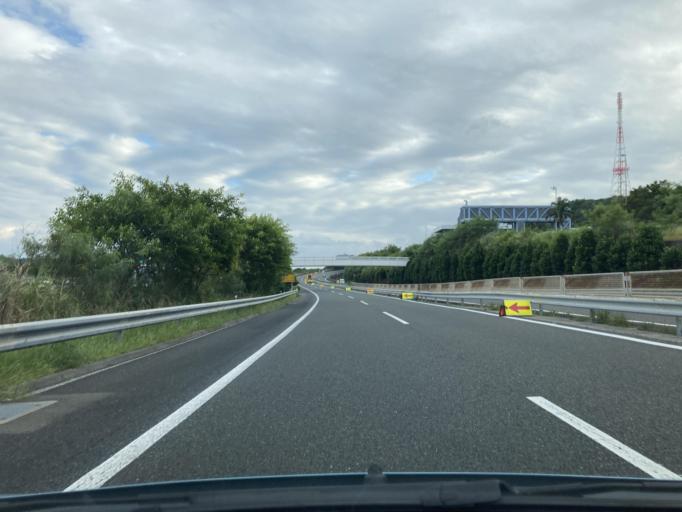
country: JP
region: Okinawa
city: Ginowan
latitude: 26.2225
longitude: 127.7384
